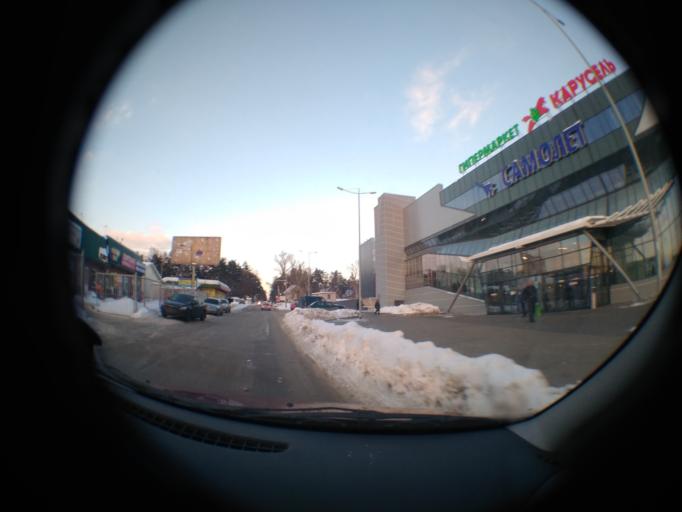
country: RU
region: Moskovskaya
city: Bykovo
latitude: 55.6104
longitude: 38.0872
